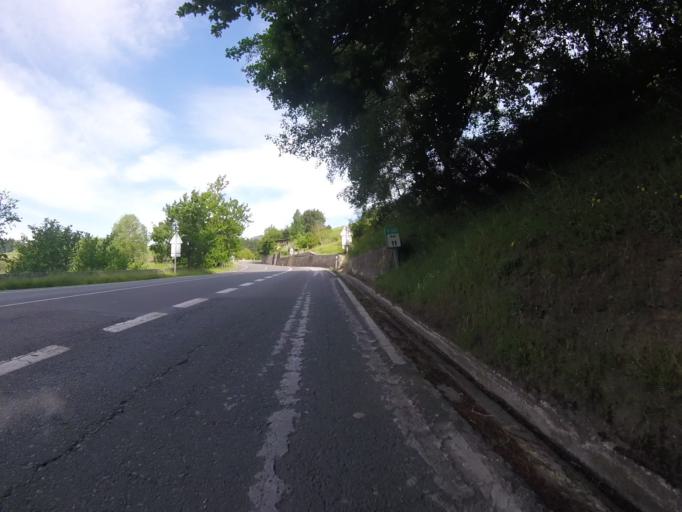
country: ES
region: Basque Country
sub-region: Provincia de Guipuzcoa
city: Zumarraga
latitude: 43.0831
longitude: -2.3024
